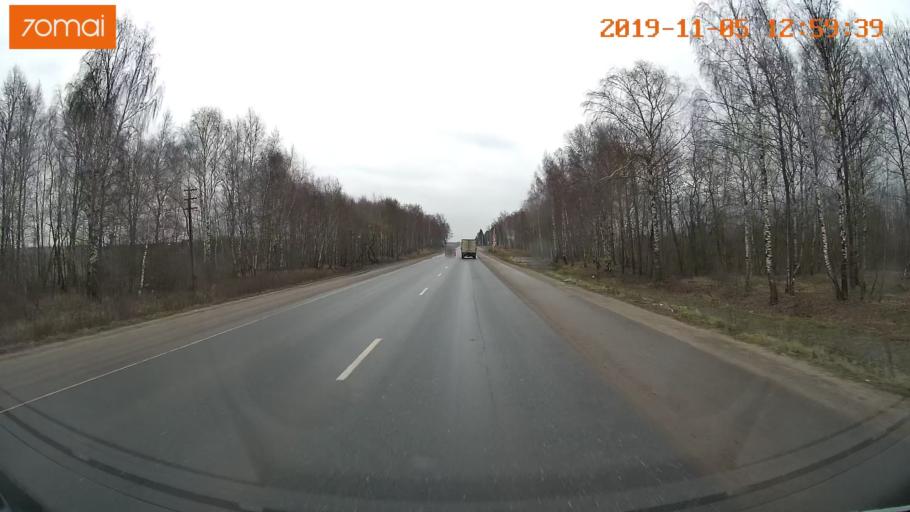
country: RU
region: Ivanovo
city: Kokhma
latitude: 56.9174
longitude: 41.1329
